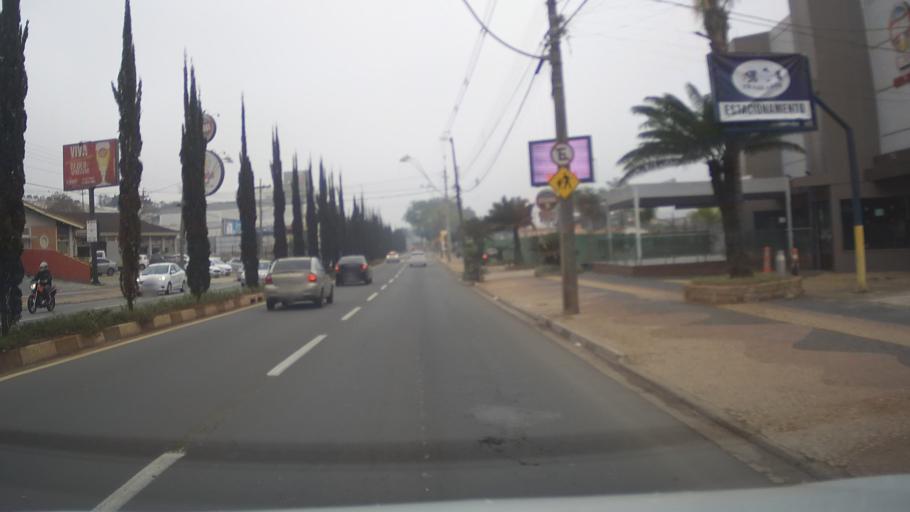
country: BR
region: Sao Paulo
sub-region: Itatiba
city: Itatiba
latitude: -23.0212
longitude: -46.8425
